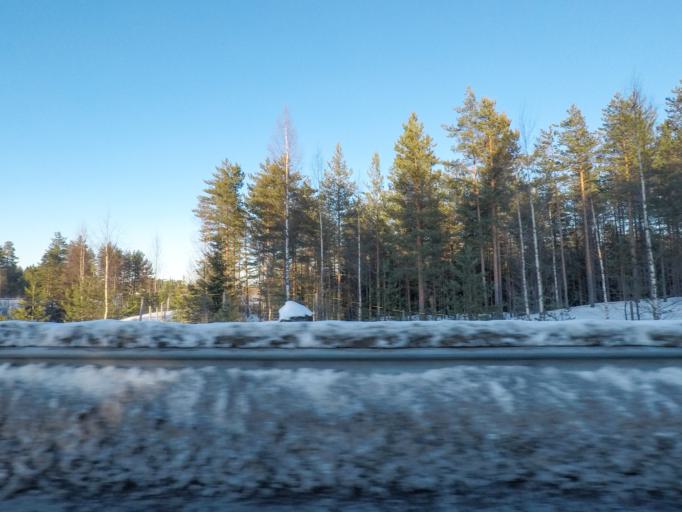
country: FI
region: Southern Savonia
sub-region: Mikkeli
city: Pertunmaa
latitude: 61.4187
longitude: 26.4346
